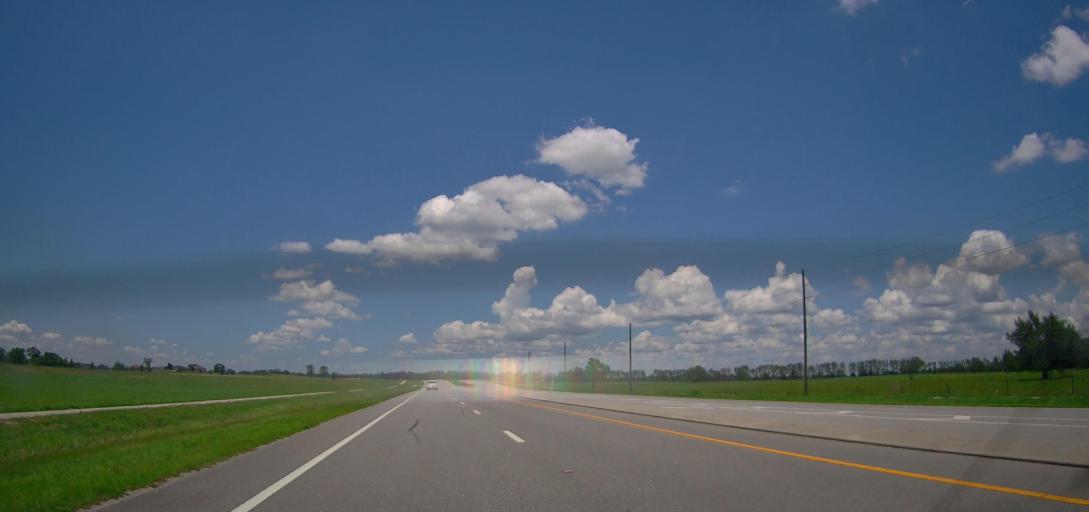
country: US
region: Florida
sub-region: Marion County
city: Silver Springs Shores
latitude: 29.0814
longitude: -82.0387
